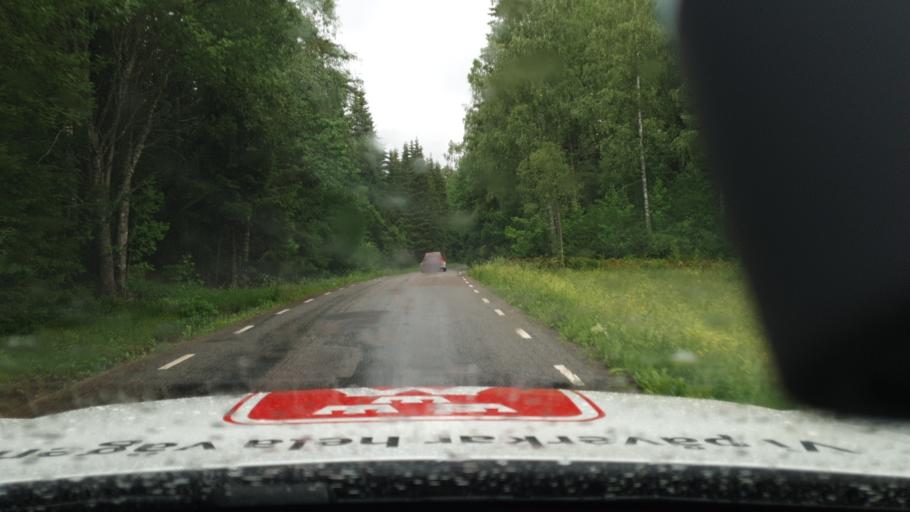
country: SE
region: Joenkoeping
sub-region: Mullsjo Kommun
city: Mullsjoe
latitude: 57.9607
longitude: 13.6675
